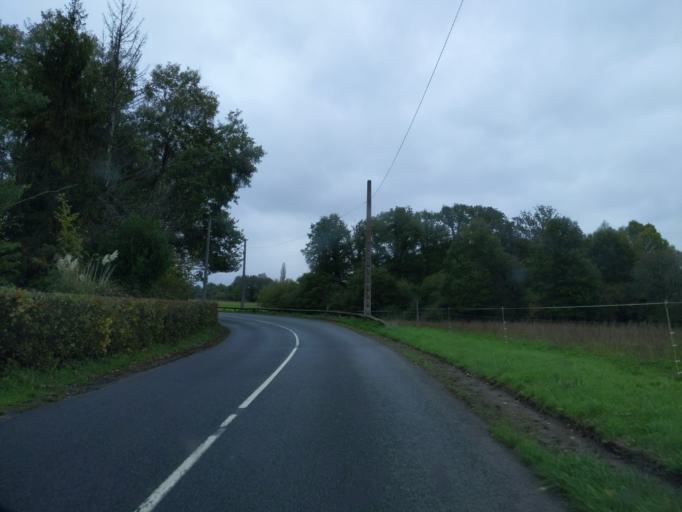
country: FR
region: Ile-de-France
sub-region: Departement des Yvelines
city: Bullion
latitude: 48.6124
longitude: 1.9792
